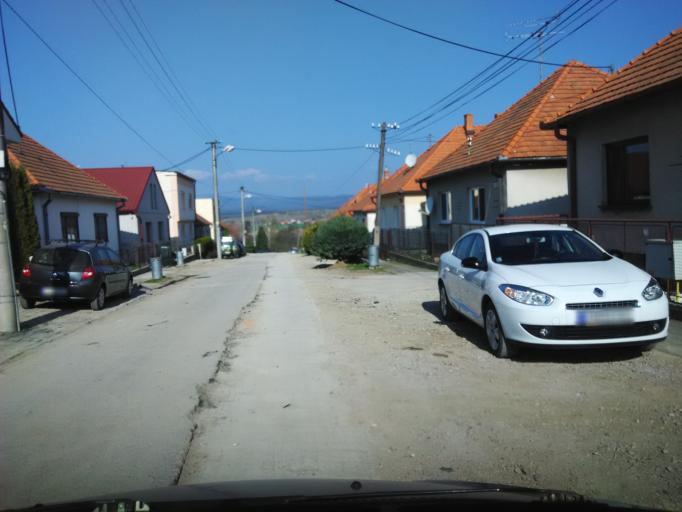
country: SK
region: Nitriansky
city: Zlate Moravce
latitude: 48.4018
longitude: 18.4254
